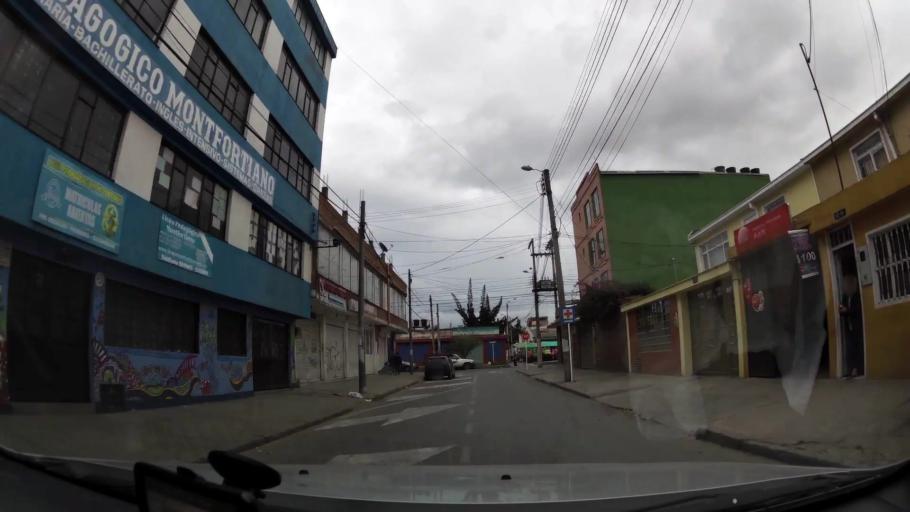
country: CO
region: Bogota D.C.
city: Bogota
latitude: 4.5933
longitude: -74.1406
